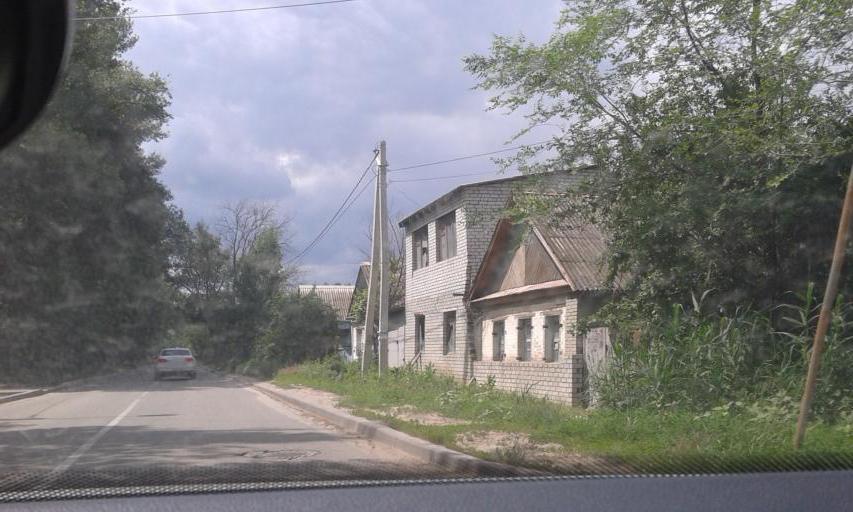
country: RU
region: Volgograd
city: Gorodishche
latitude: 48.7726
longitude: 44.4923
